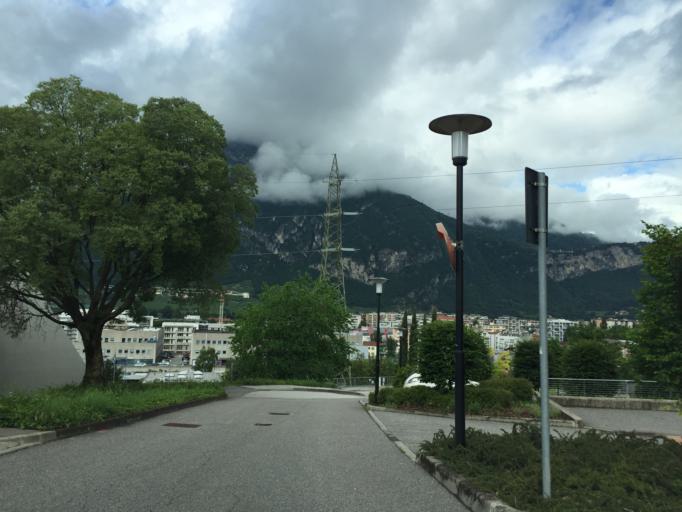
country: IT
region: Trentino-Alto Adige
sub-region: Provincia di Trento
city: Ravina
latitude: 46.0471
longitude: 11.1333
